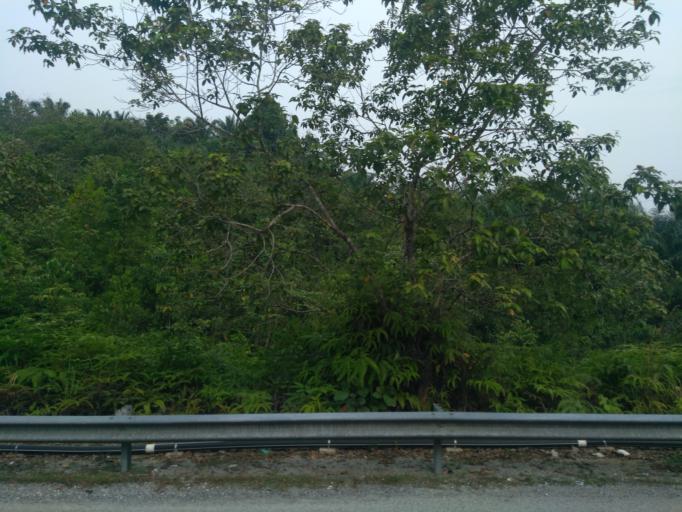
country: MY
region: Perak
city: Ipoh
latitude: 4.5550
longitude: 101.1674
